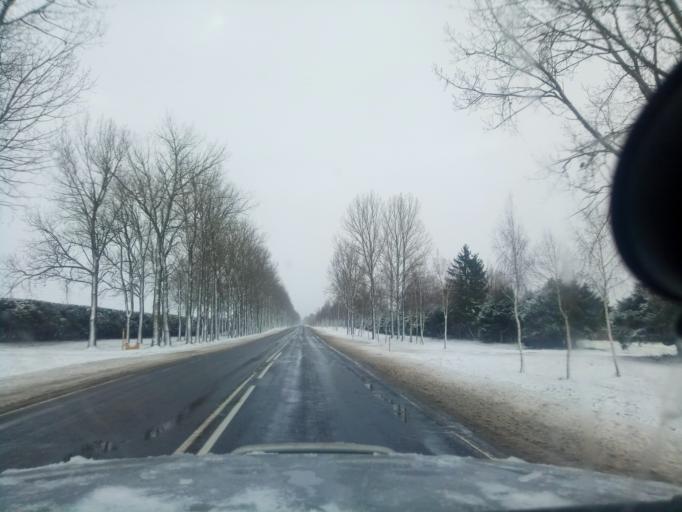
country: BY
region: Minsk
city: Haradzyeya
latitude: 53.3486
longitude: 26.5178
